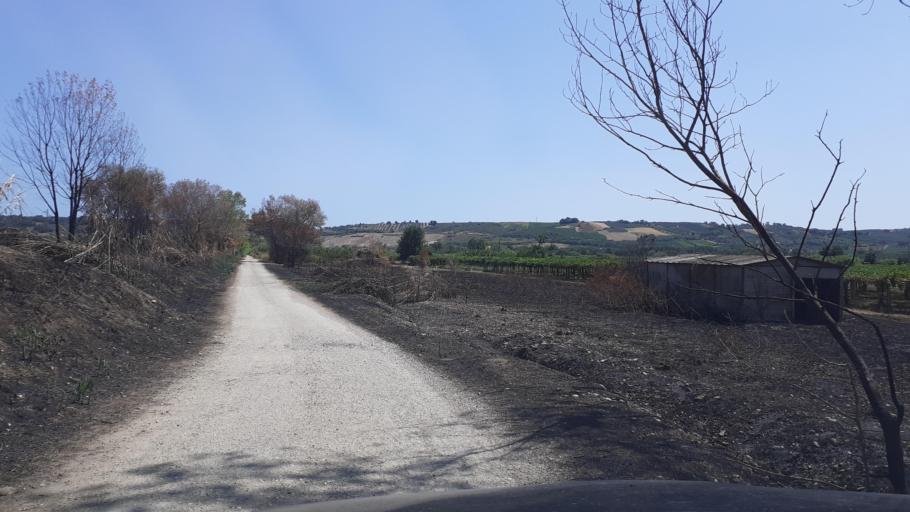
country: IT
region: Abruzzo
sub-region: Provincia di Chieti
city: Fossacesia
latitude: 42.2118
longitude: 14.4951
